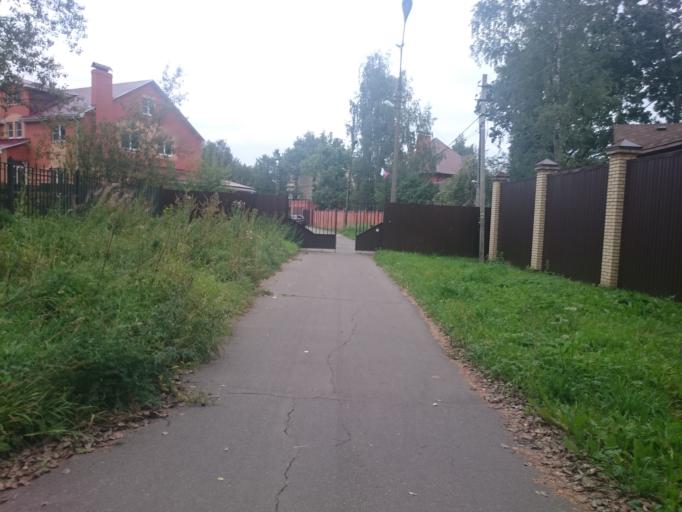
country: RU
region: Moskovskaya
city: Novopodrezkovo
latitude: 55.8948
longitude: 37.3563
